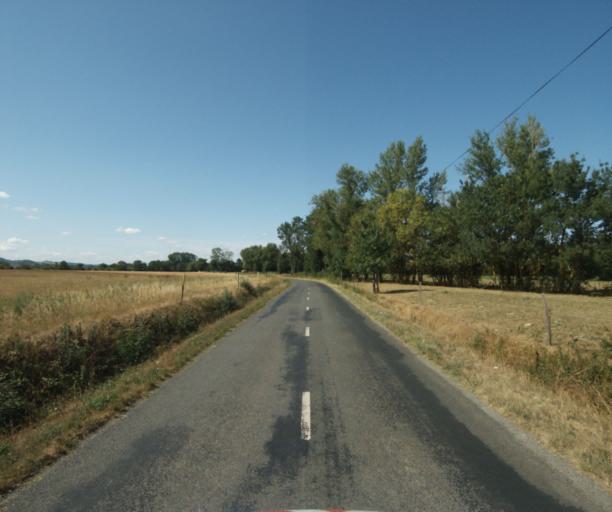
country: FR
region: Midi-Pyrenees
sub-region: Departement de la Haute-Garonne
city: Revel
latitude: 43.4782
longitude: 1.9904
